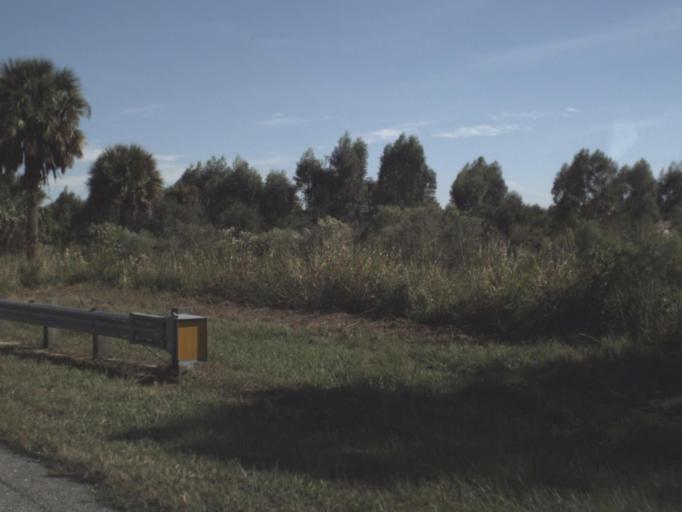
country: US
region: Florida
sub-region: Glades County
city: Moore Haven
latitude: 26.9045
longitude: -81.2588
